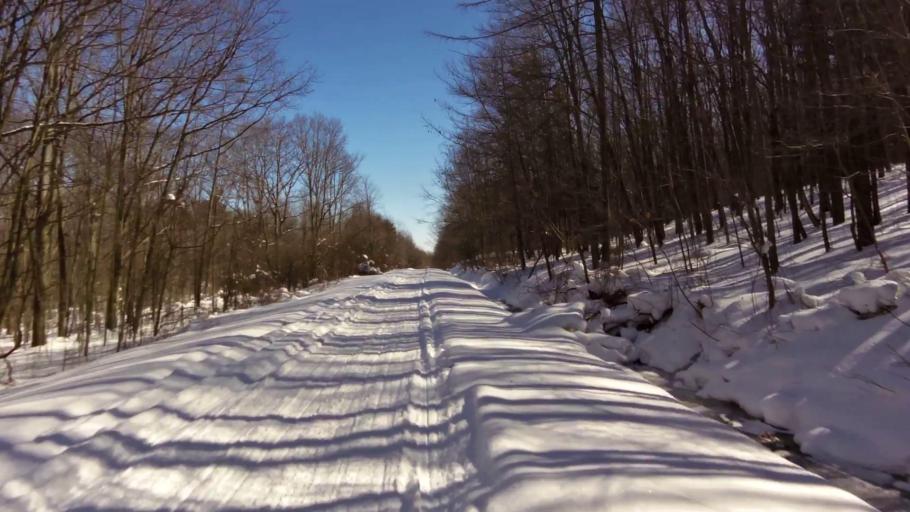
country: US
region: New York
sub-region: Allegany County
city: Cuba
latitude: 42.3072
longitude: -78.2340
